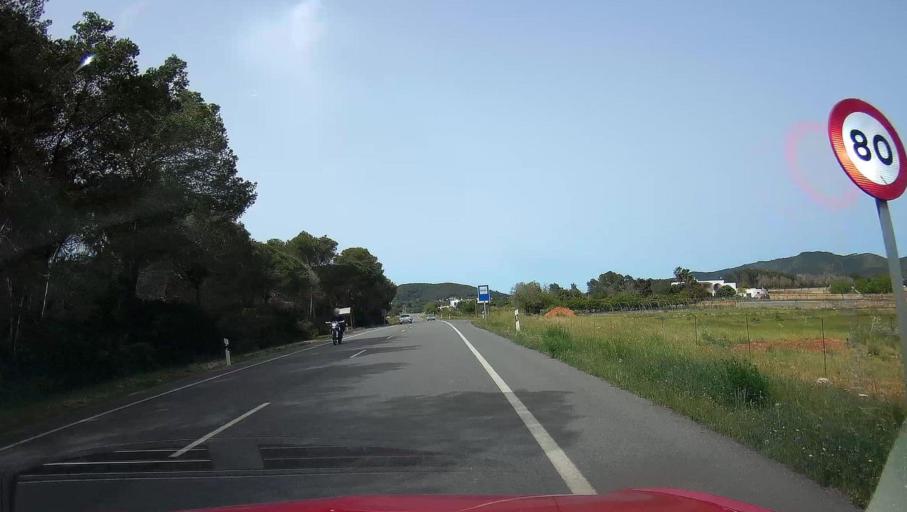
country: ES
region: Balearic Islands
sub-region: Illes Balears
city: Santa Eularia des Riu
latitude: 39.0168
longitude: 1.4877
